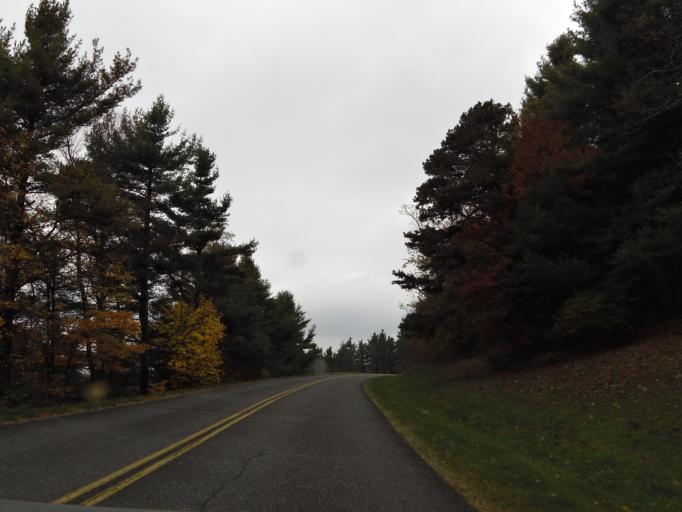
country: US
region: North Carolina
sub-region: Ashe County
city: West Jefferson
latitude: 36.2906
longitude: -81.4052
